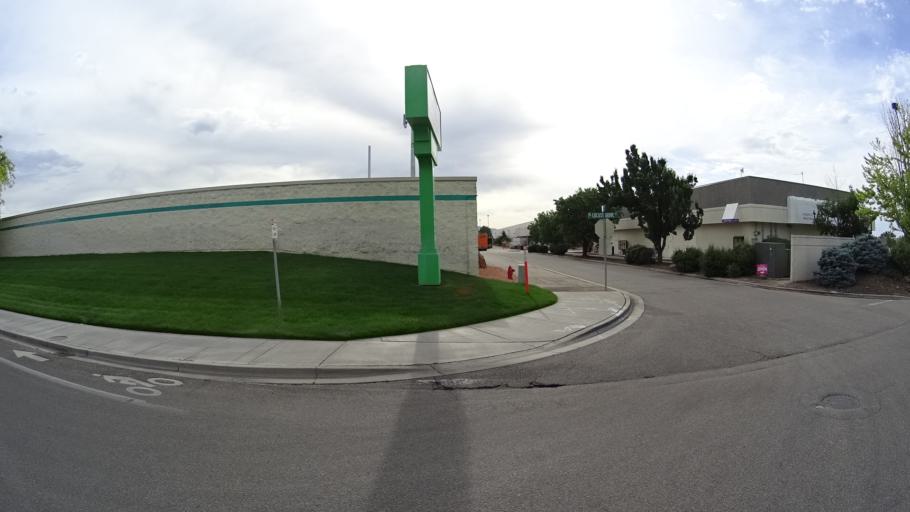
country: US
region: Idaho
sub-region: Ada County
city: Meridian
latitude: 43.6219
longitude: -116.3745
